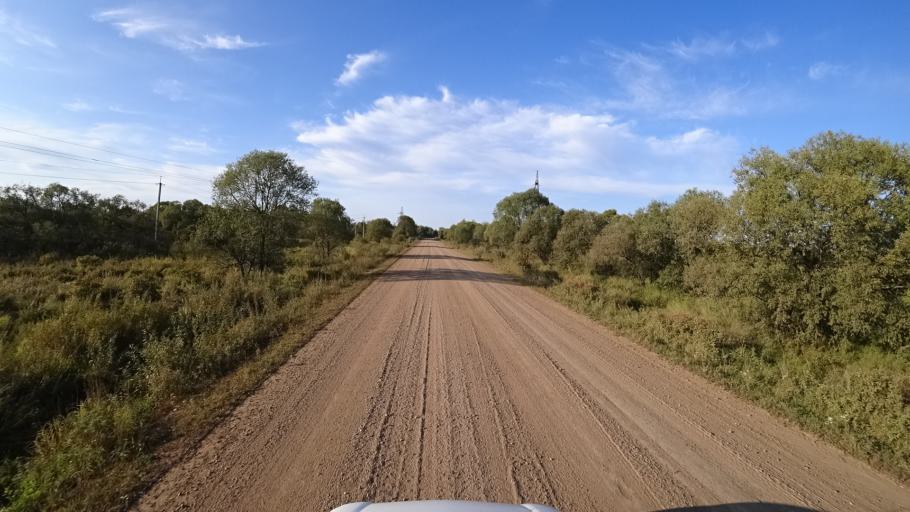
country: RU
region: Amur
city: Arkhara
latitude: 49.3645
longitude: 130.1364
